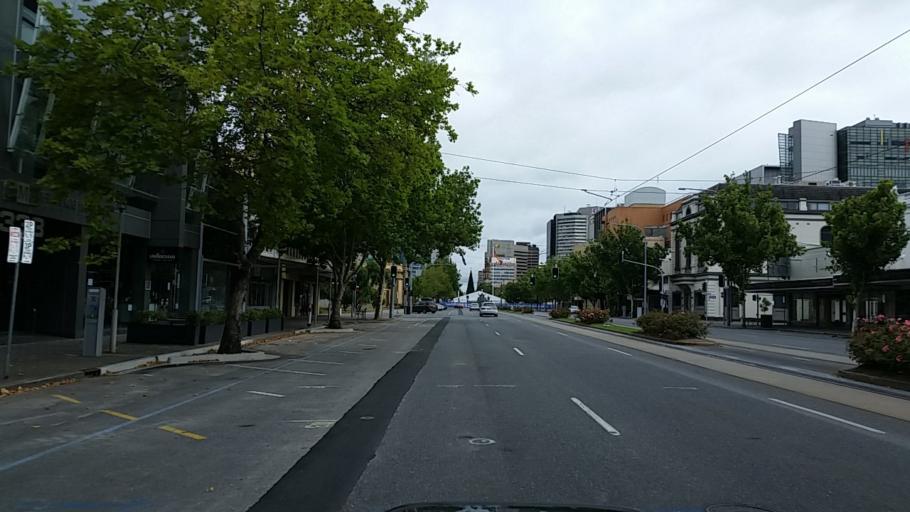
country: AU
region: South Australia
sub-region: Adelaide
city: Adelaide
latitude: -34.9322
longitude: 138.6001
